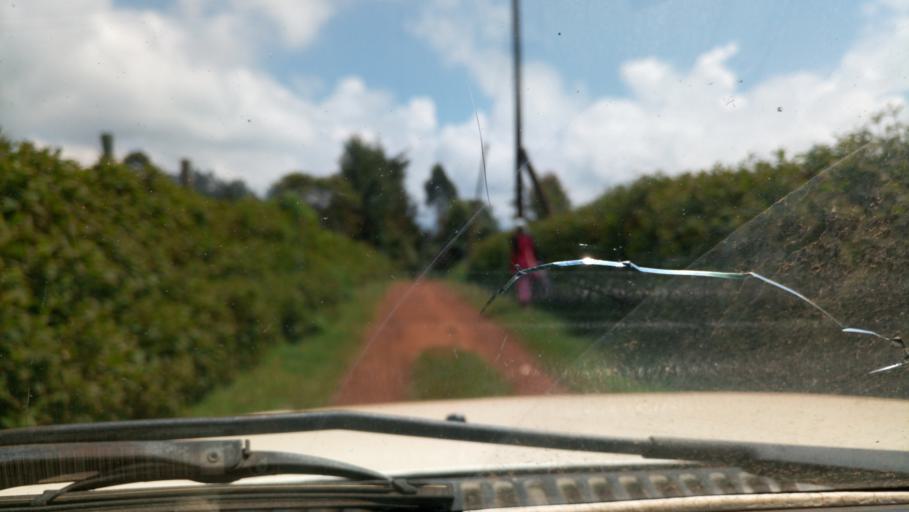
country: KE
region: Nyeri
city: Othaya
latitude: -0.6264
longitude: 36.8401
